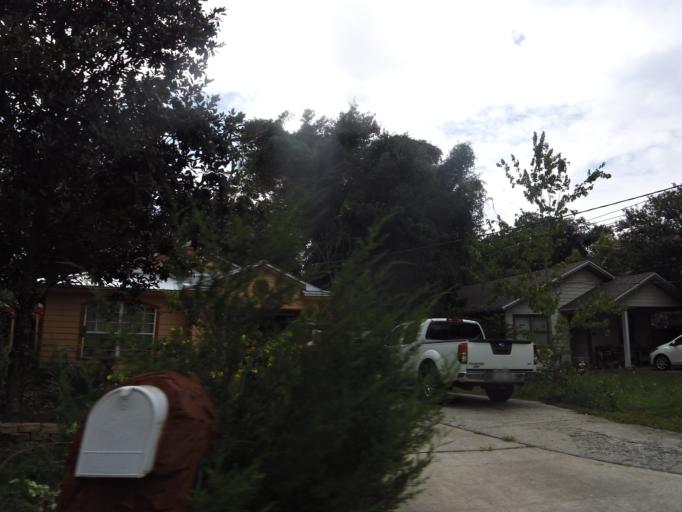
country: US
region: Florida
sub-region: Duval County
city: Atlantic Beach
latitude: 30.3279
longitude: -81.4207
